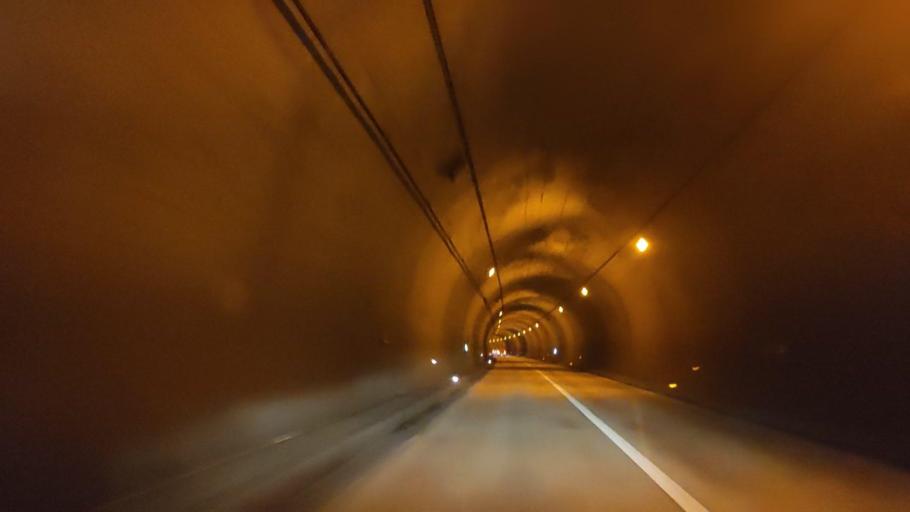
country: JP
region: Tottori
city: Kurayoshi
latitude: 35.3087
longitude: 133.7472
